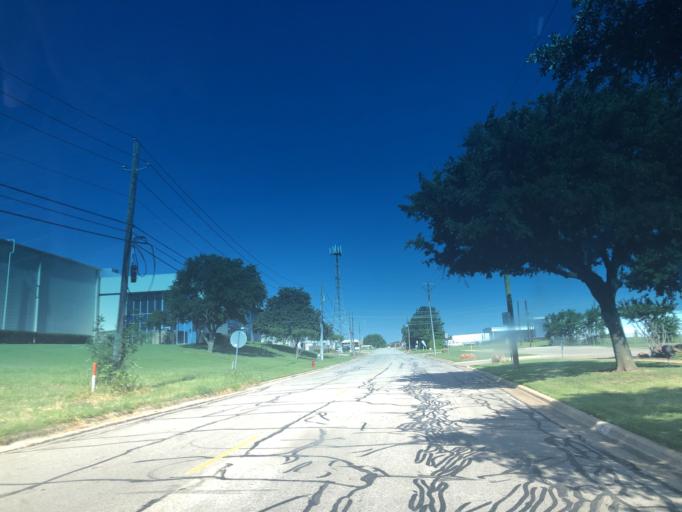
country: US
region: Texas
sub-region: Dallas County
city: Grand Prairie
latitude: 32.7164
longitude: -97.0460
